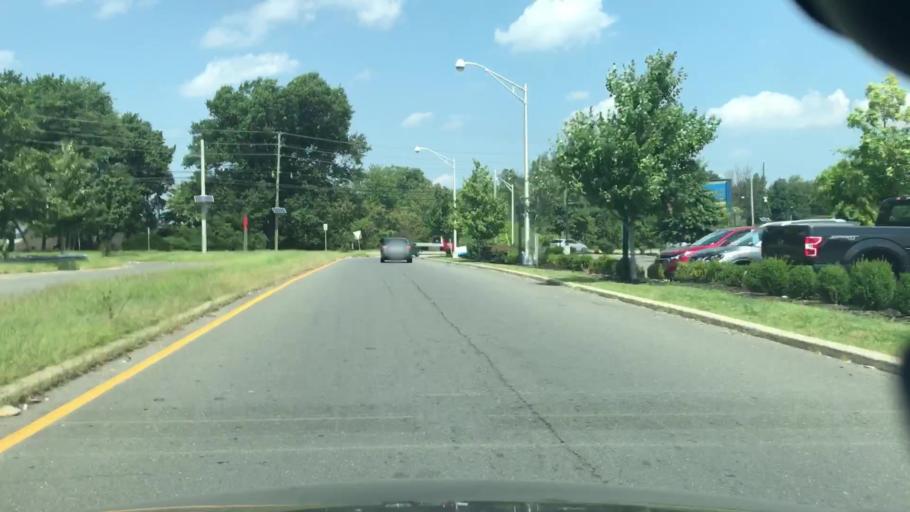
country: US
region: New Jersey
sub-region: Middlesex County
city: Metuchen
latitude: 40.5309
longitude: -74.3792
